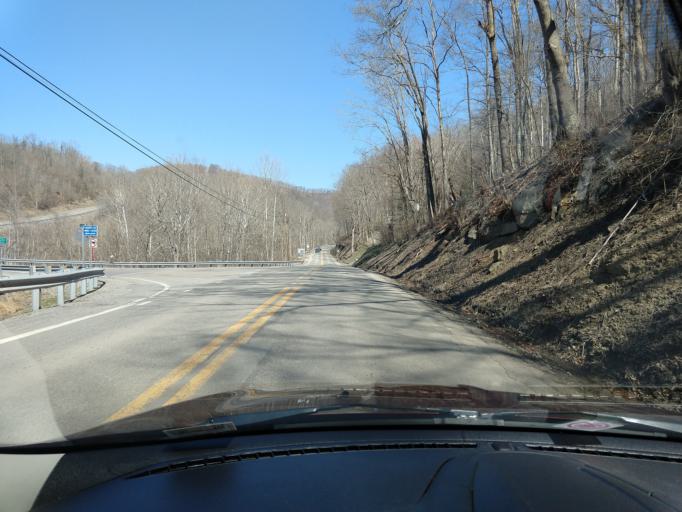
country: US
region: West Virginia
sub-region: Braxton County
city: Sutton
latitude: 38.6697
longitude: -80.7166
